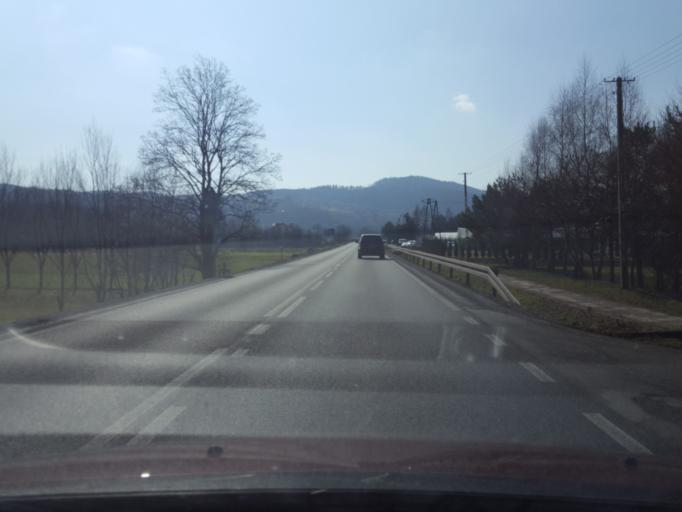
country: PL
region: Lesser Poland Voivodeship
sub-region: Powiat brzeski
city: Czchow
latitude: 49.8276
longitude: 20.6779
